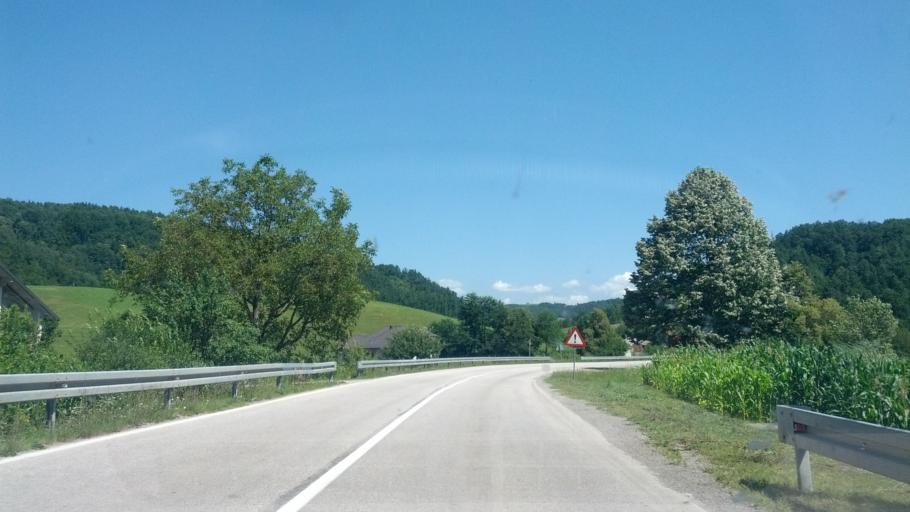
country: BA
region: Federation of Bosnia and Herzegovina
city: Bosanska Krupa
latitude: 44.9223
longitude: 16.1465
